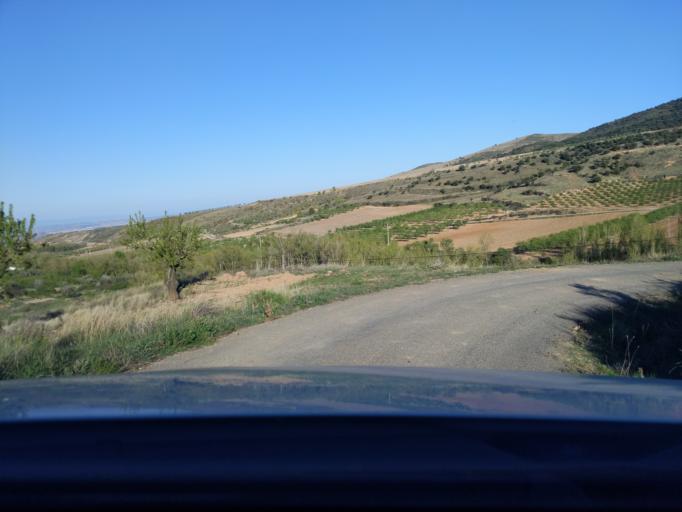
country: ES
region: La Rioja
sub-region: Provincia de La Rioja
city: Bergasa
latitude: 42.2487
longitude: -2.1371
